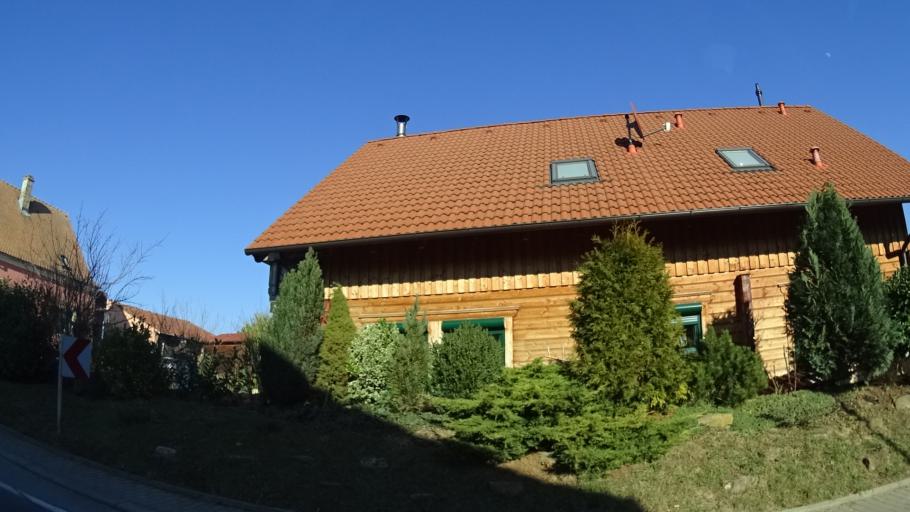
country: DE
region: Rheinland-Pfalz
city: Dackenheim
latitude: 49.5231
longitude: 8.1835
